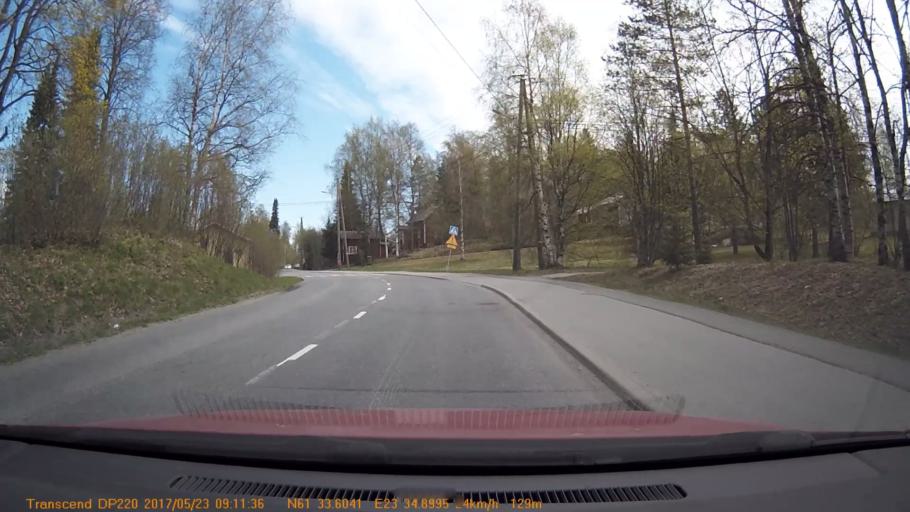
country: FI
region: Pirkanmaa
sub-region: Tampere
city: Yloejaervi
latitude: 61.5600
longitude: 23.5816
